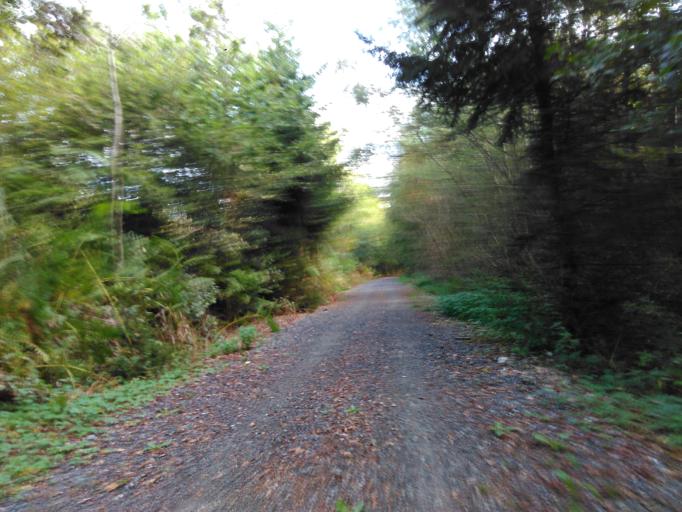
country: BE
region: Wallonia
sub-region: Province du Luxembourg
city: Vaux-sur-Sure
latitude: 49.9386
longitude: 5.5717
